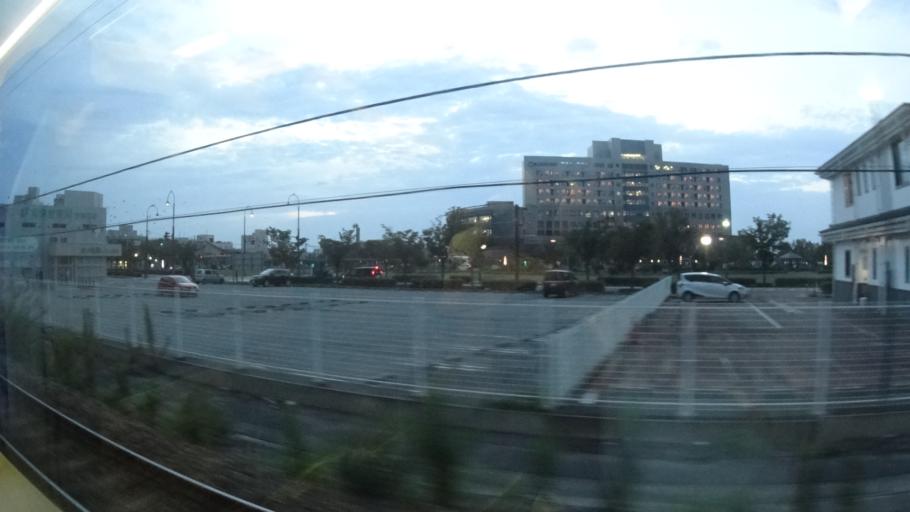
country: JP
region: Niigata
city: Shibata
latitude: 37.9456
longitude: 139.3366
